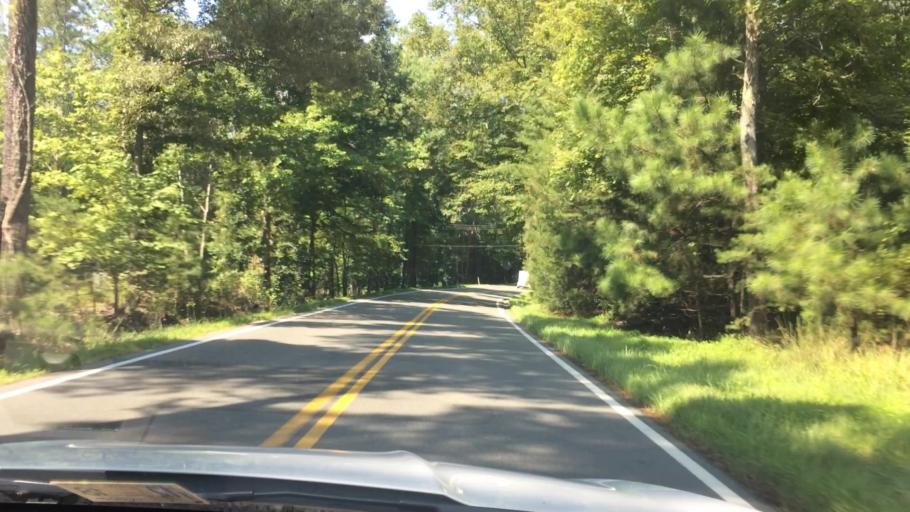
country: US
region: Virginia
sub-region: New Kent County
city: New Kent
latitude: 37.5145
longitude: -76.9890
